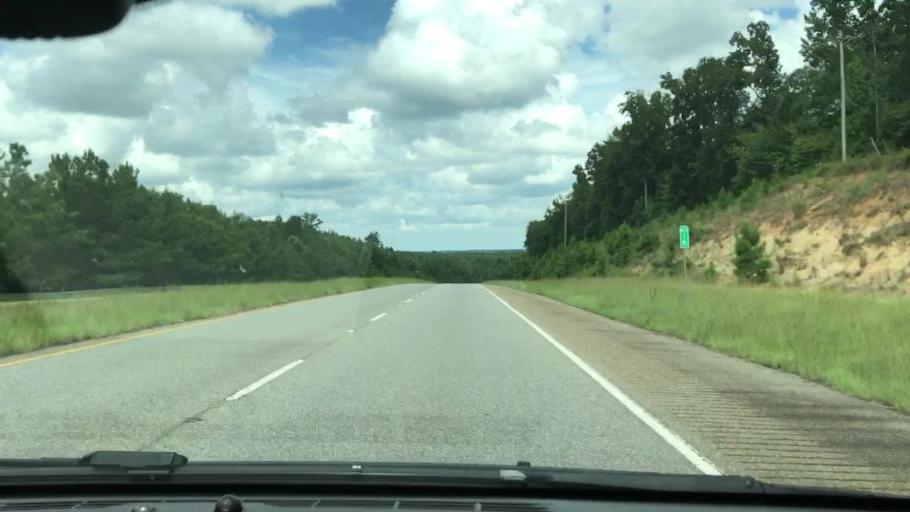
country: US
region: Georgia
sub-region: Stewart County
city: Lumpkin
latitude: 32.1221
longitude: -84.8191
